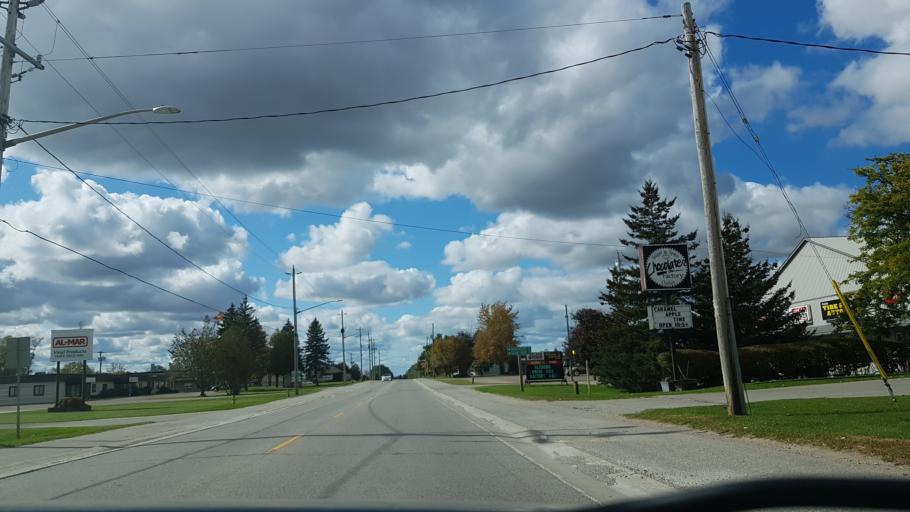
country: CA
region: Ontario
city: South Huron
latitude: 43.3614
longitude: -81.4873
